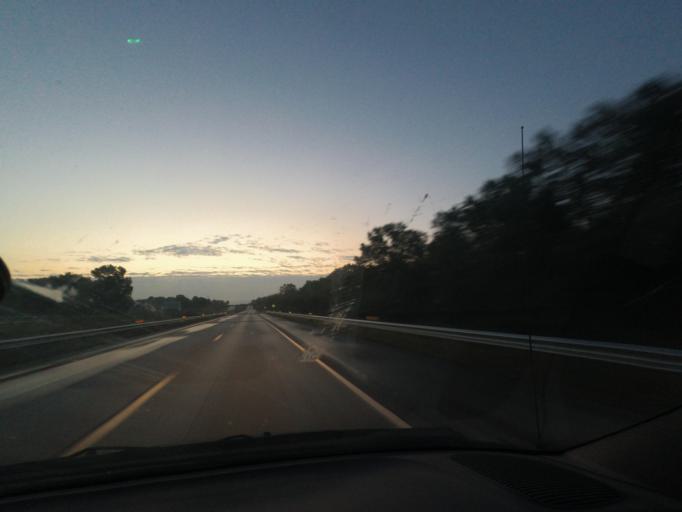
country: US
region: Missouri
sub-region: Linn County
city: Brookfield
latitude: 39.7787
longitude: -93.1489
